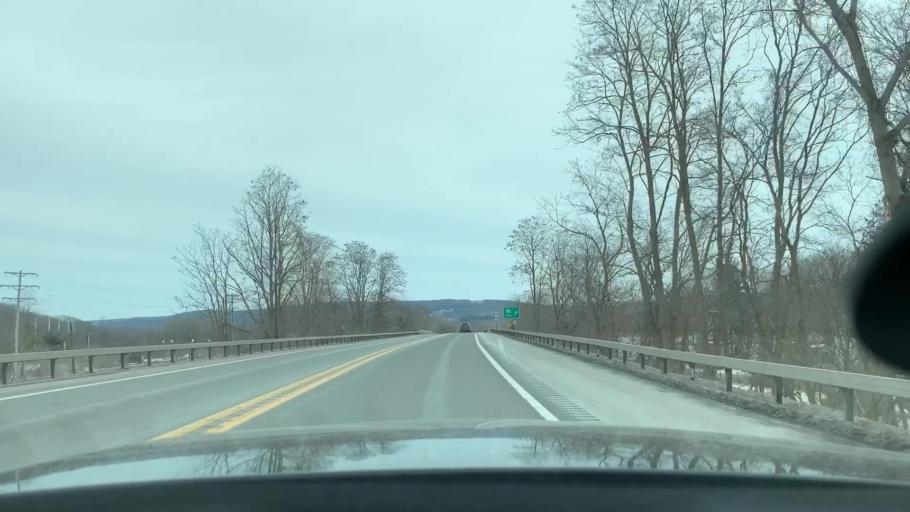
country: US
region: New York
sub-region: Herkimer County
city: Ilion
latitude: 43.0210
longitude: -75.0328
